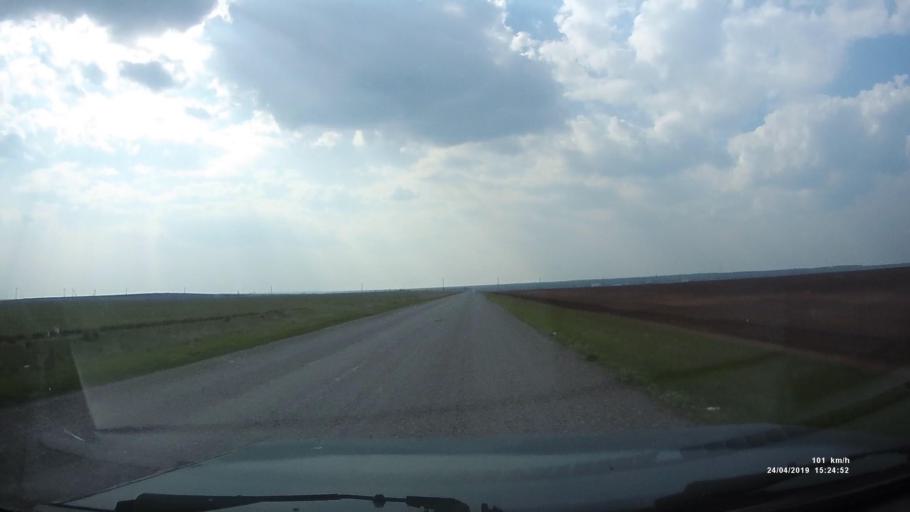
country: RU
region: Rostov
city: Remontnoye
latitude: 46.5498
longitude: 43.0595
